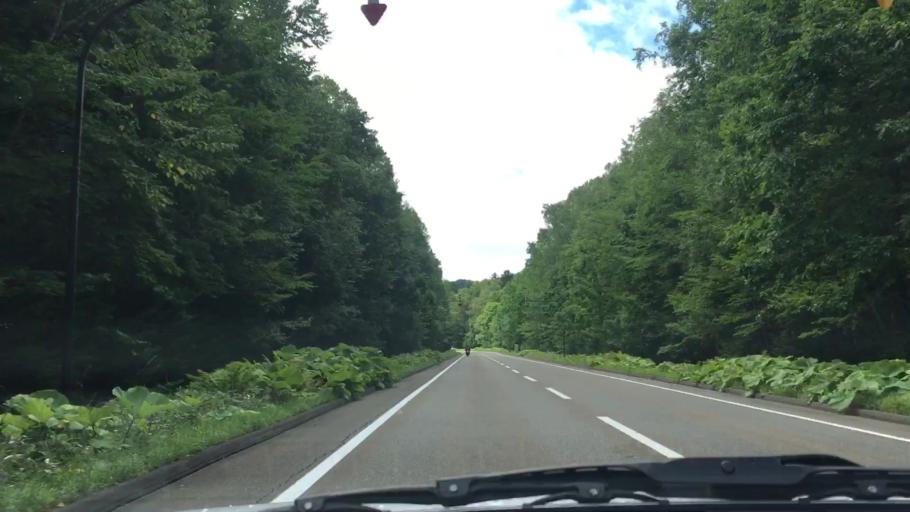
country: JP
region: Hokkaido
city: Kitami
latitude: 43.4002
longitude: 143.9283
